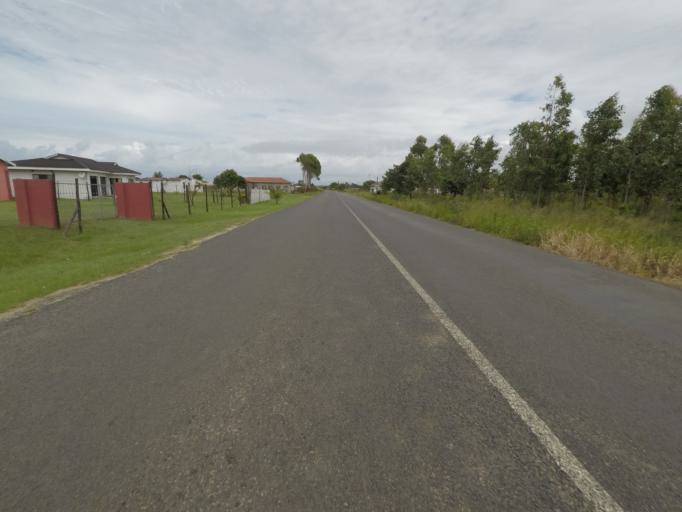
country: ZA
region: KwaZulu-Natal
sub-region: uThungulu District Municipality
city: eSikhawini
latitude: -28.9048
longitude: 31.8859
